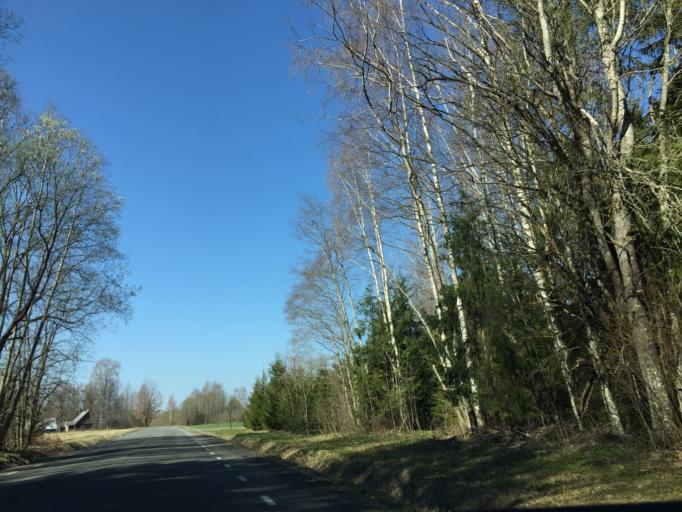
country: EE
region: Tartu
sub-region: Alatskivi vald
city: Kallaste
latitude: 58.5765
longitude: 26.9338
